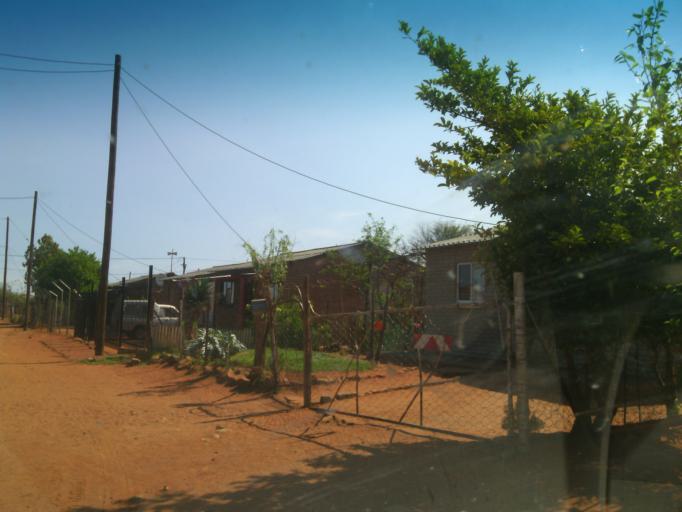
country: ZA
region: Northern Cape
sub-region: Frances Baard District Municipality
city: Barkly West
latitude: -28.5180
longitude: 24.5036
